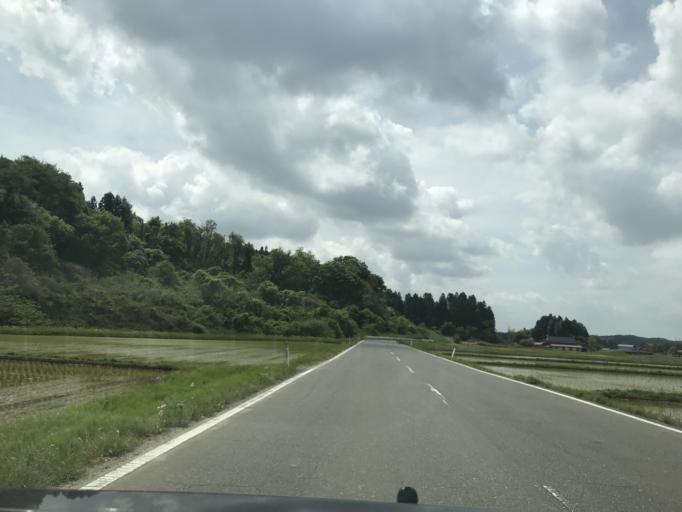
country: JP
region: Iwate
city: Ichinoseki
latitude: 38.8380
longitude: 141.0188
